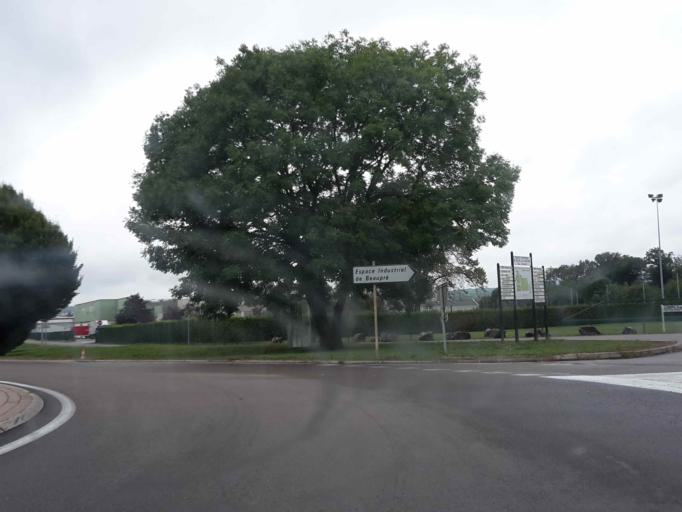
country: FR
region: Franche-Comte
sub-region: Departement du Doubs
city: Thise
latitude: 47.2741
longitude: 6.1037
